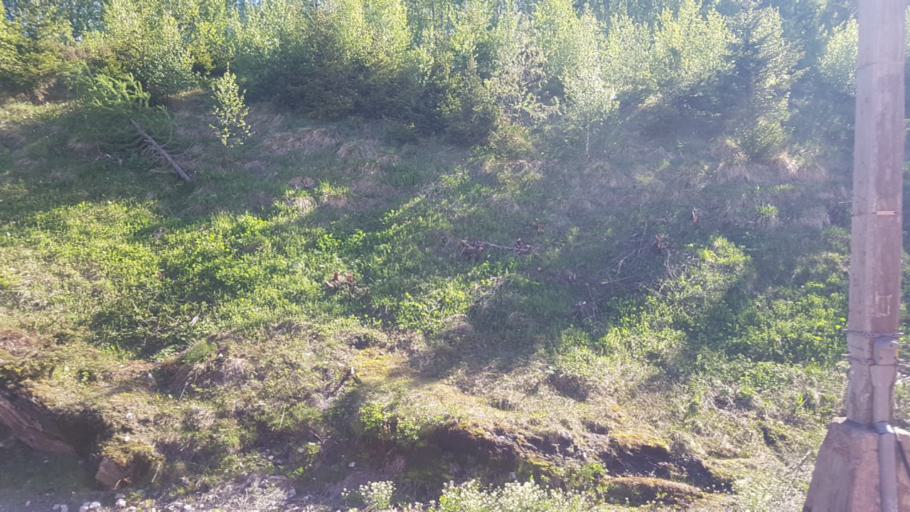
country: NO
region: Sor-Trondelag
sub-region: Rennebu
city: Berkak
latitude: 62.8244
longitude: 10.0105
